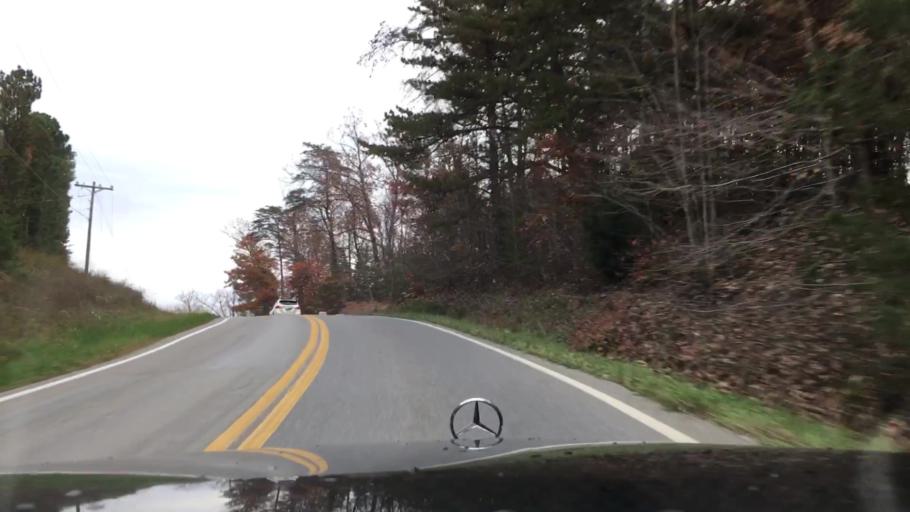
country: US
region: Virginia
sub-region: Campbell County
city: Timberlake
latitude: 37.2569
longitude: -79.2750
